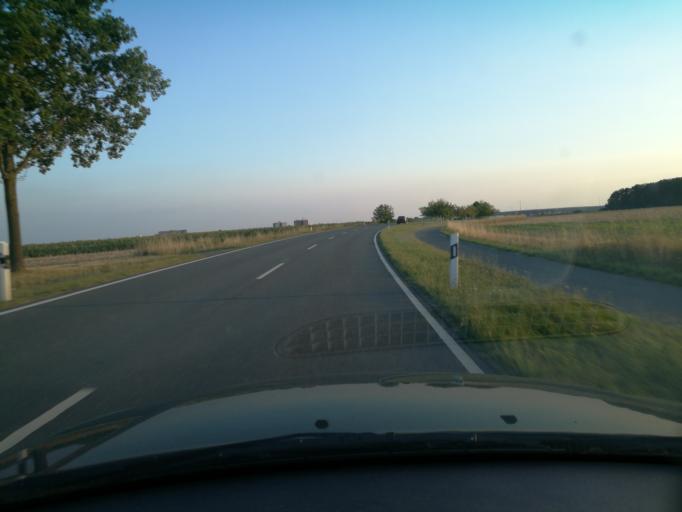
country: DE
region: Bavaria
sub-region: Regierungsbezirk Mittelfranken
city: Herzogenaurach
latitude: 49.5871
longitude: 10.8902
